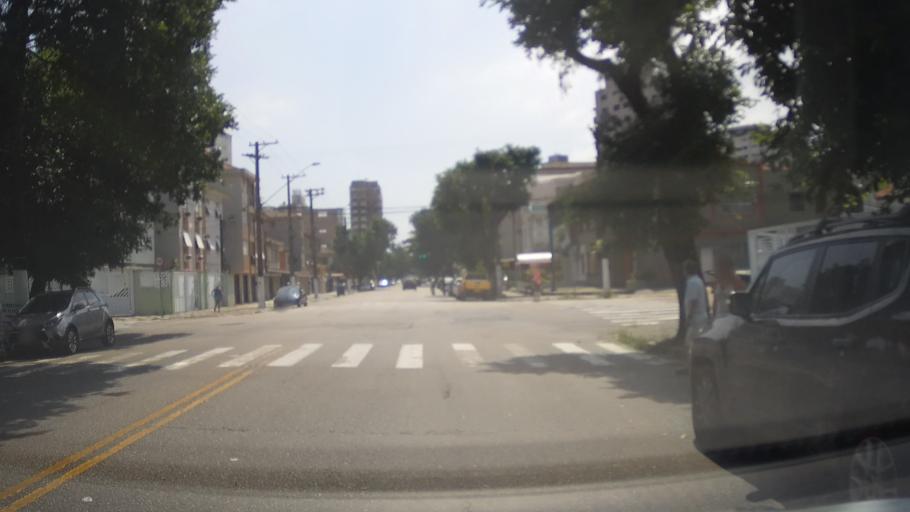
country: BR
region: Sao Paulo
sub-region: Santos
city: Santos
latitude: -23.9859
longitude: -46.3026
